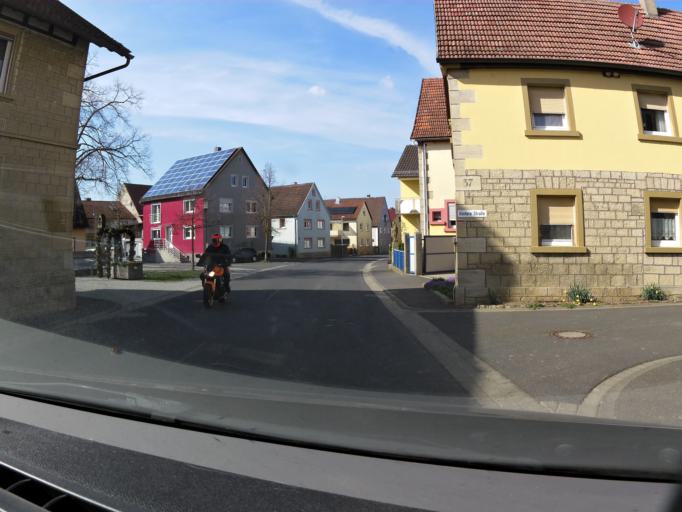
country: DE
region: Bavaria
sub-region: Regierungsbezirk Unterfranken
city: Bieberehren
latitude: 49.5140
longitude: 10.0085
